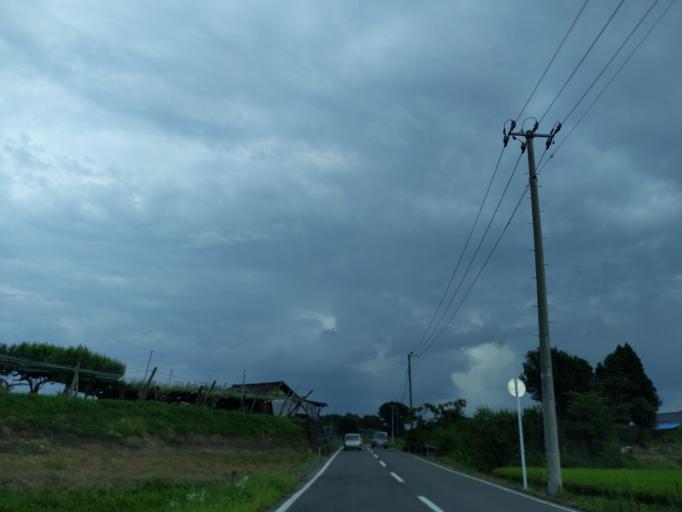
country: JP
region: Fukushima
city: Sukagawa
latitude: 37.3123
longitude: 140.3343
